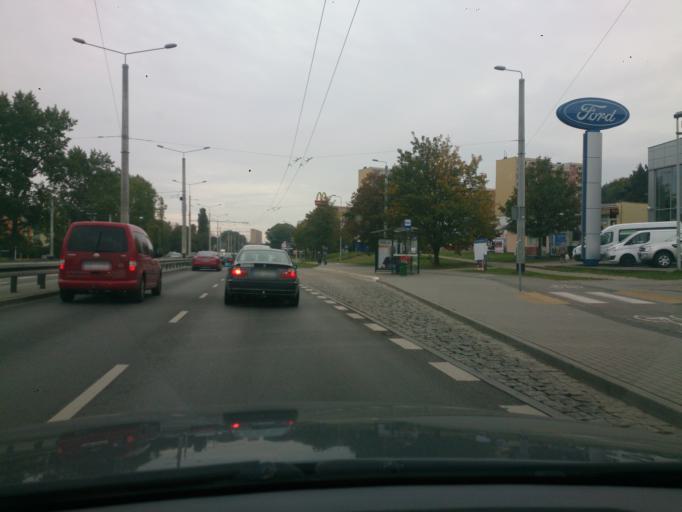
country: PL
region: Pomeranian Voivodeship
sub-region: Gdynia
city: Pogorze
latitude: 54.5462
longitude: 18.4416
